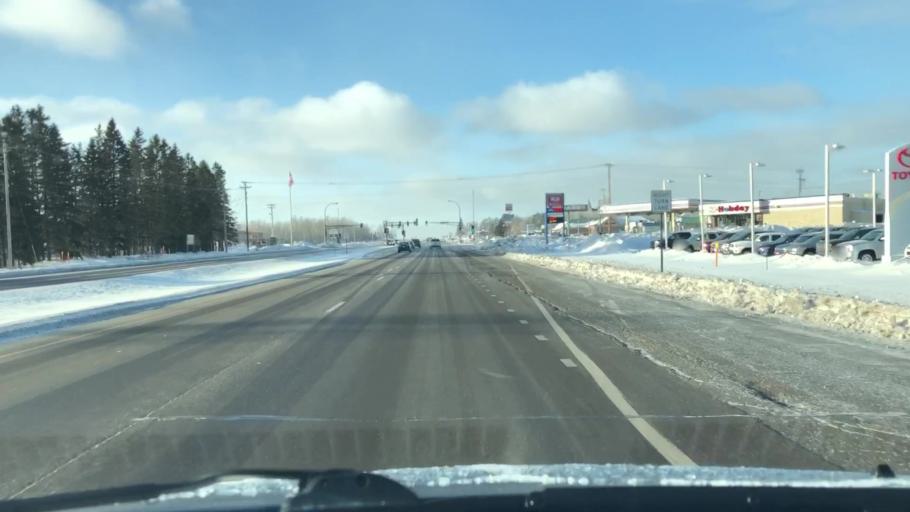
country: US
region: Minnesota
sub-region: Saint Louis County
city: Hermantown
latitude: 46.8208
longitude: -92.1844
